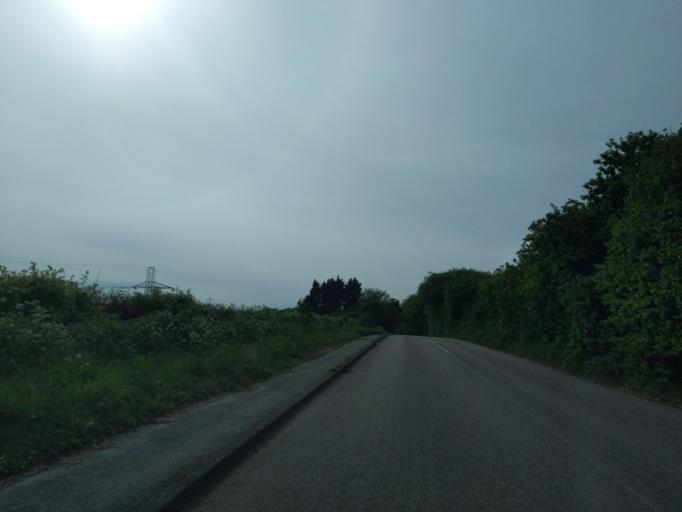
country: GB
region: England
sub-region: Devon
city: Yelverton
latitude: 50.4443
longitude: -4.0909
